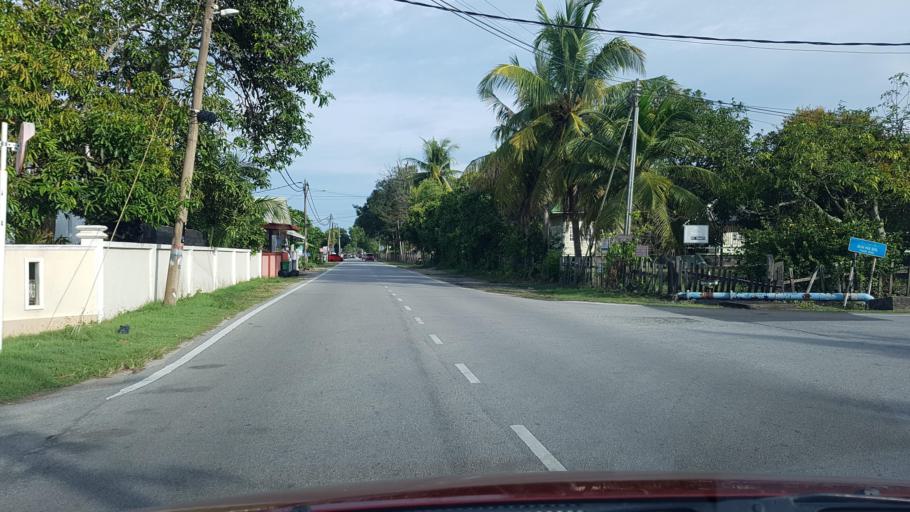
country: MY
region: Terengganu
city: Kuala Terengganu
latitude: 5.3172
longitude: 103.1568
